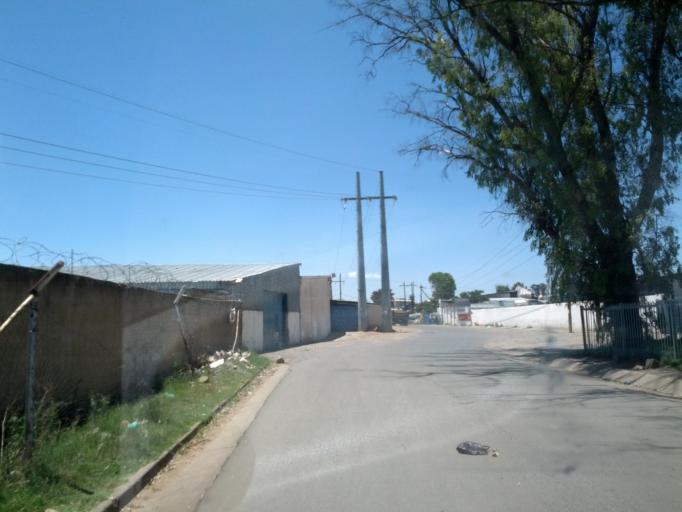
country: LS
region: Maseru
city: Maseru
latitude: -29.2971
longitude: 27.4667
